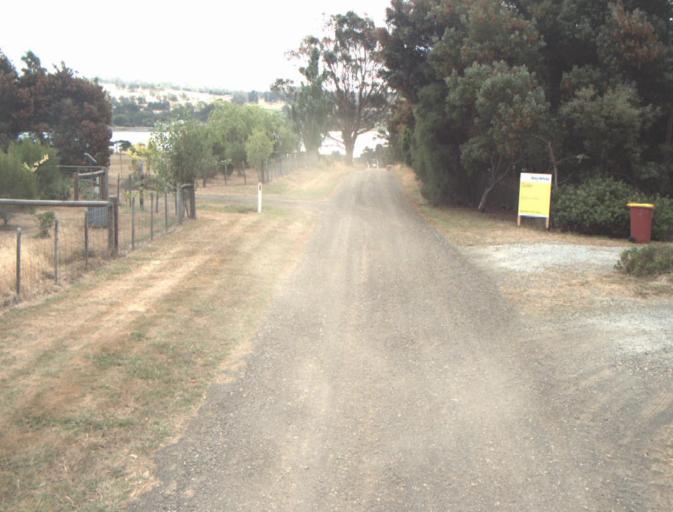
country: AU
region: Tasmania
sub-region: Launceston
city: Mayfield
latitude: -41.2966
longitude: 146.9863
